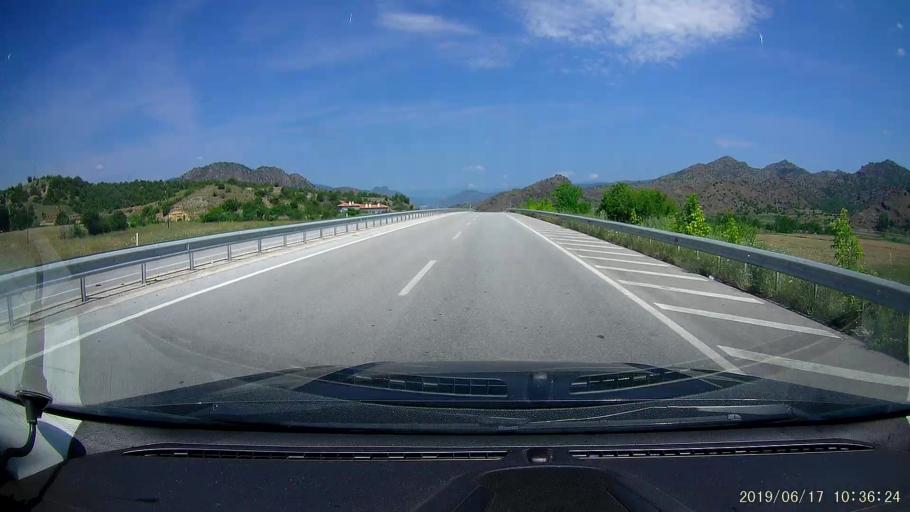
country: TR
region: Corum
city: Osmancik
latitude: 40.9786
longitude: 34.6821
